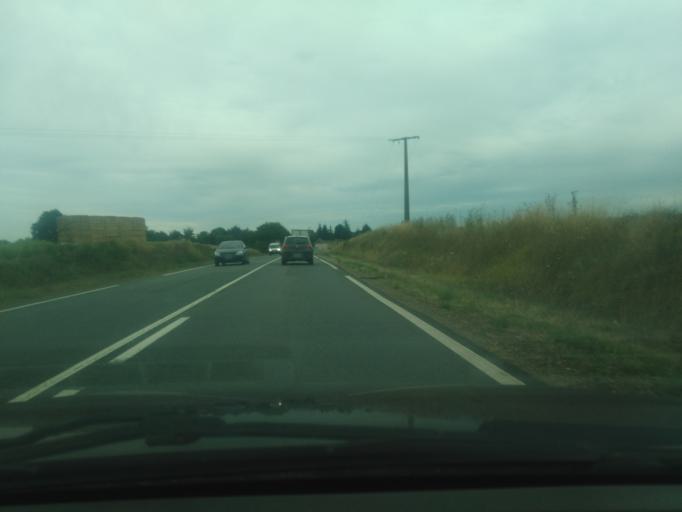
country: FR
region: Poitou-Charentes
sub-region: Departement de la Vienne
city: Saint-Savin
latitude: 46.5681
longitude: 0.8490
